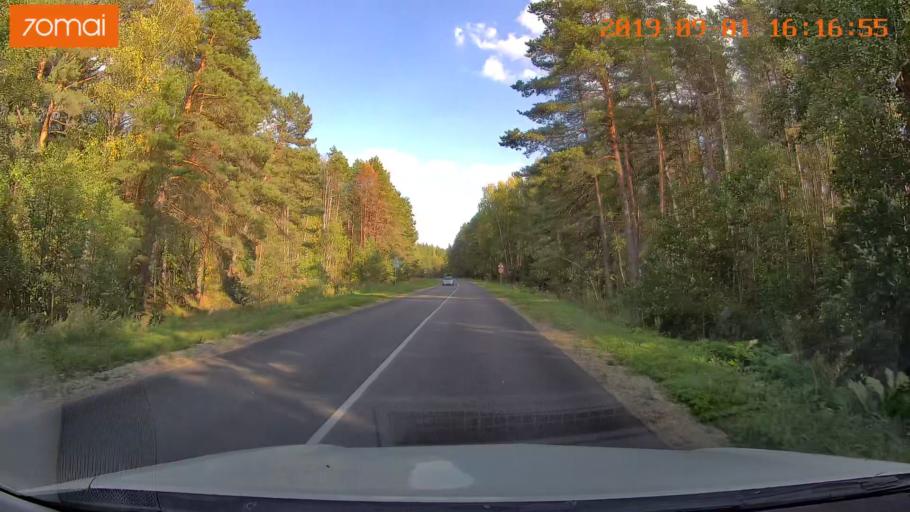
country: RU
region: Kaluga
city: Maloyaroslavets
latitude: 54.9118
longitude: 36.4990
